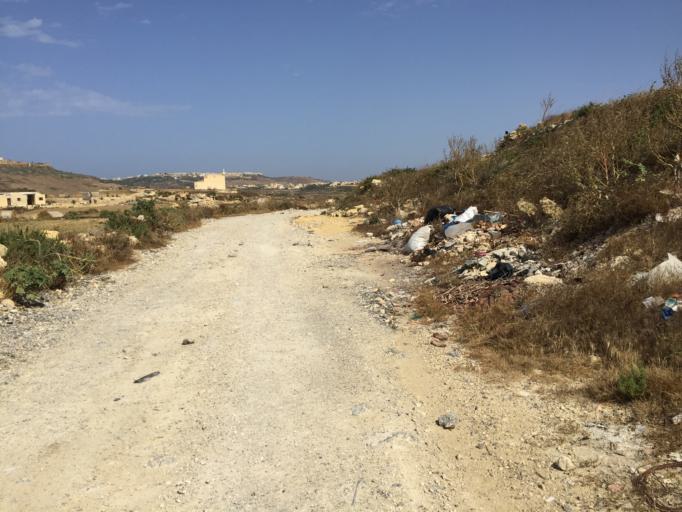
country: MT
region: L-Gharb
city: Gharb
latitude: 36.0717
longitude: 14.2017
